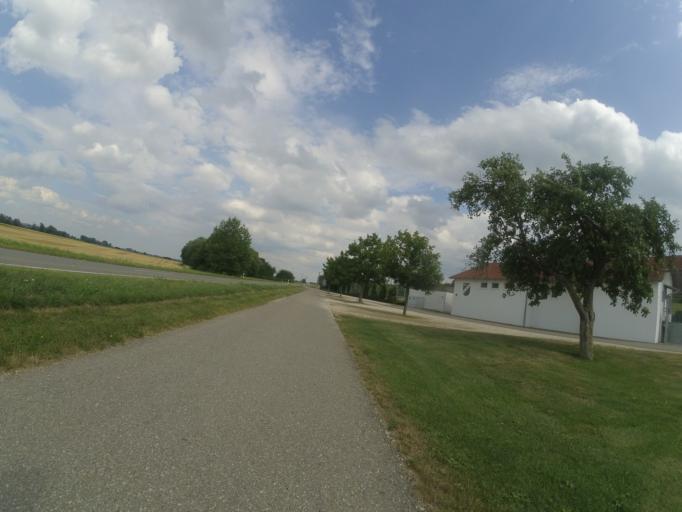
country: DE
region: Baden-Wuerttemberg
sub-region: Tuebingen Region
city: Griesingen
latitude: 48.2716
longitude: 9.7735
